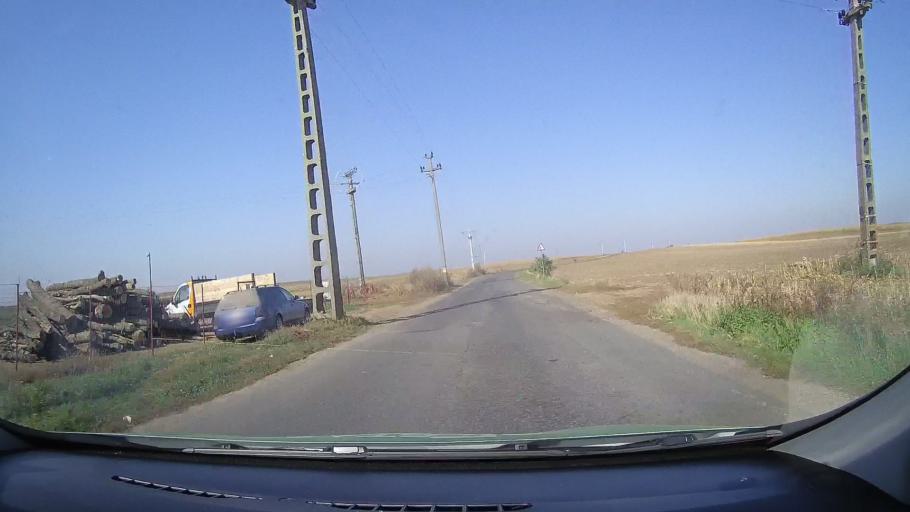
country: RO
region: Satu Mare
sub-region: Comuna Petresti
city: Petresti
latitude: 47.6099
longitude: 22.3550
